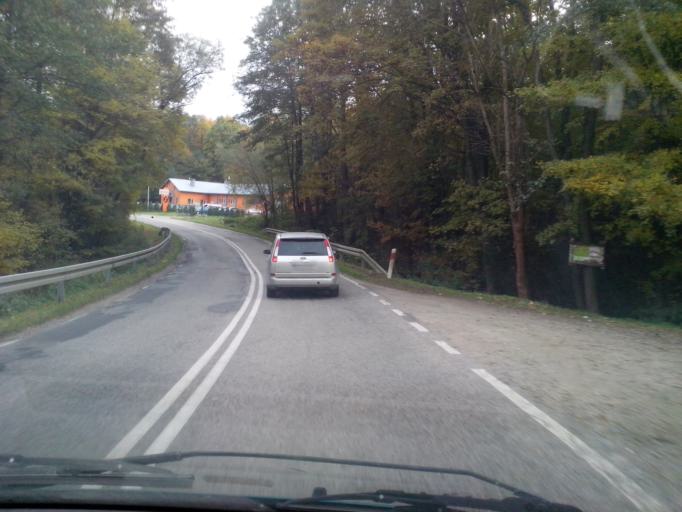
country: PL
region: Subcarpathian Voivodeship
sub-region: Powiat strzyzowski
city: Wisniowa
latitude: 49.8784
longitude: 21.6458
